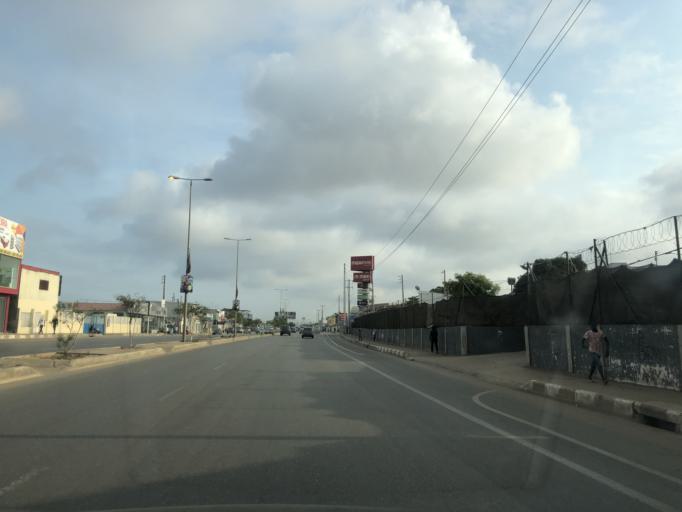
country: AO
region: Luanda
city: Luanda
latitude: -8.8777
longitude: 13.2101
